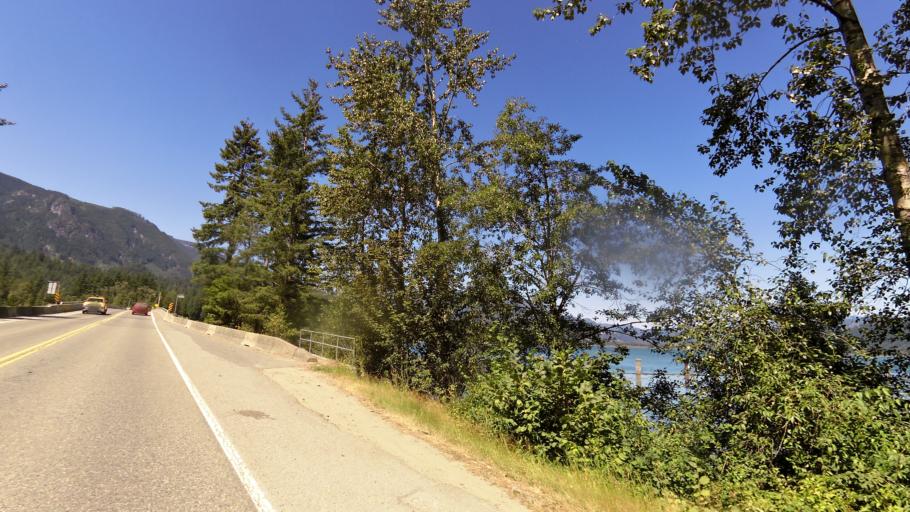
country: CA
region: British Columbia
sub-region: Fraser Valley Regional District
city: Chilliwack
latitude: 49.2458
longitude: -121.9458
